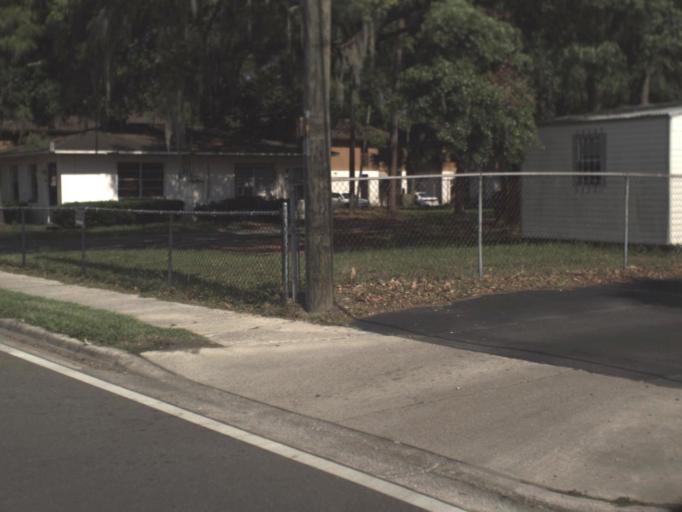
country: US
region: Florida
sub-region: Clay County
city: Bellair-Meadowbrook Terrace
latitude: 30.2821
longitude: -81.7500
